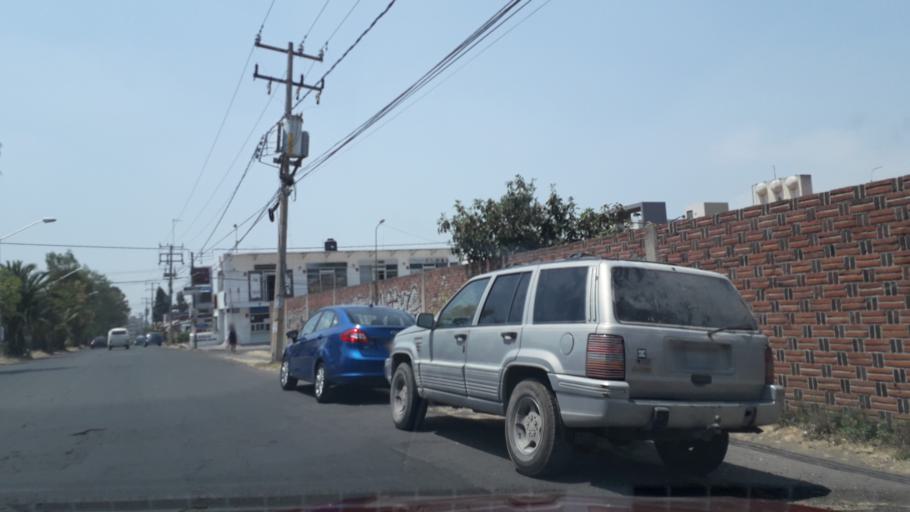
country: MX
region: Puebla
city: Puebla
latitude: 19.0543
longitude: -98.2335
